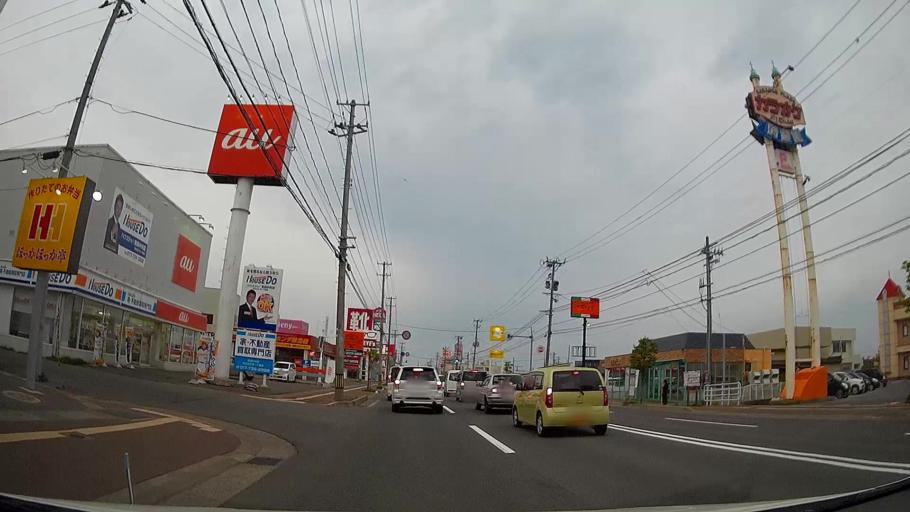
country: JP
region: Aomori
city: Aomori Shi
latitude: 40.8017
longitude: 140.7567
